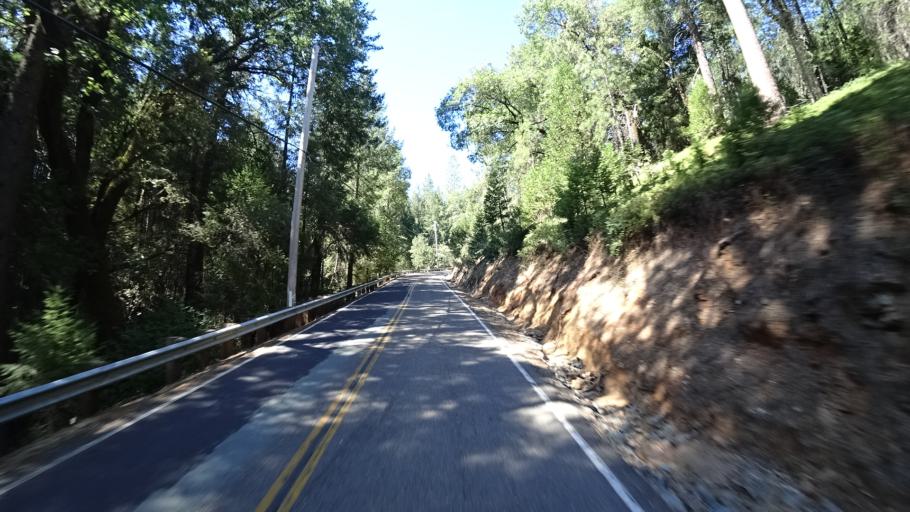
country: US
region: California
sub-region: Amador County
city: Pioneer
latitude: 38.3530
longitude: -120.5088
